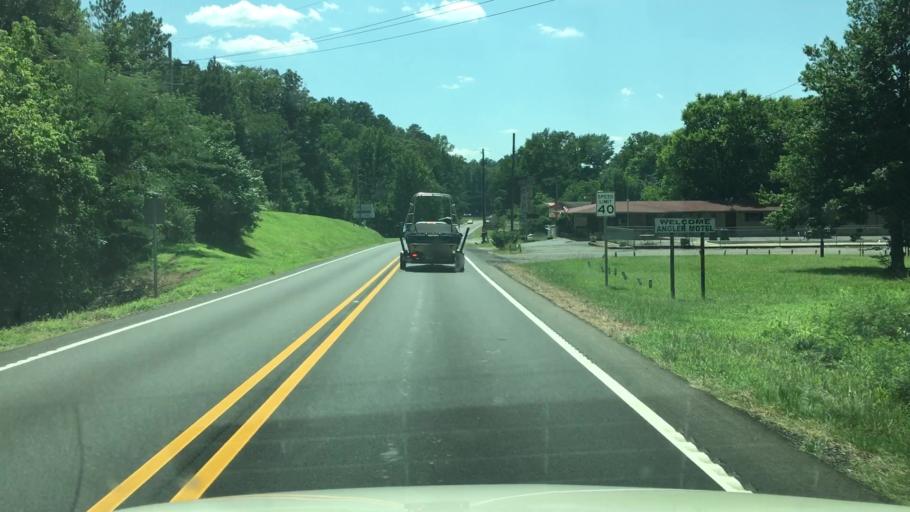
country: US
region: Arkansas
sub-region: Garland County
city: Rockwell
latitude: 34.5225
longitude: -93.3344
